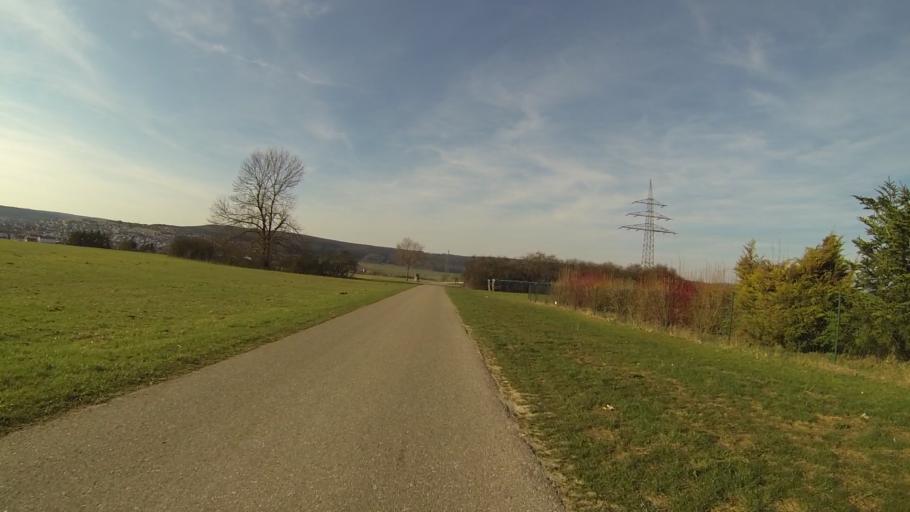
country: DE
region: Baden-Wuerttemberg
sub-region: Regierungsbezirk Stuttgart
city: Herbrechtingen
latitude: 48.6214
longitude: 10.1913
